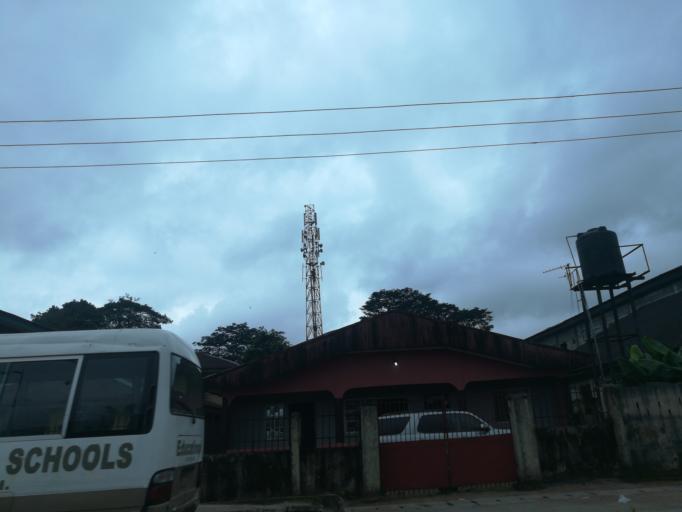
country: NG
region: Rivers
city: Port Harcourt
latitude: 4.7621
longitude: 7.0292
